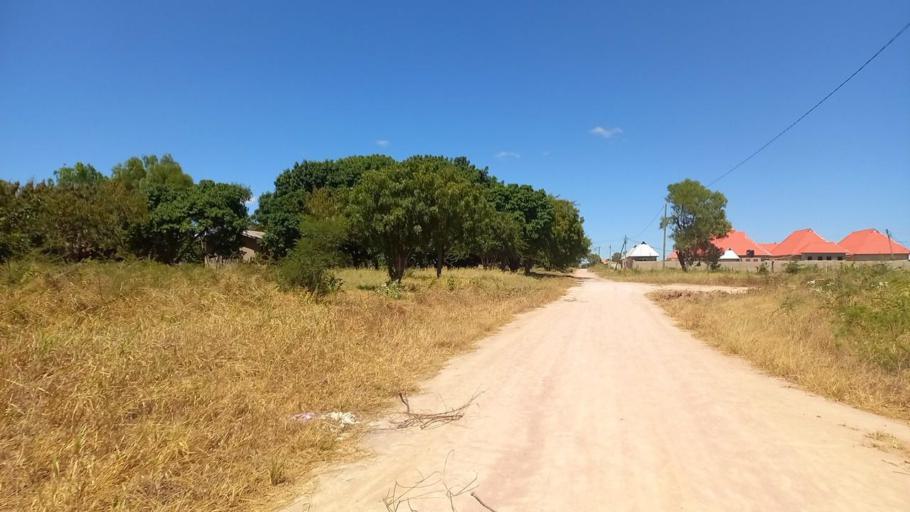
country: TZ
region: Dodoma
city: Dodoma
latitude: -6.1163
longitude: 35.7394
